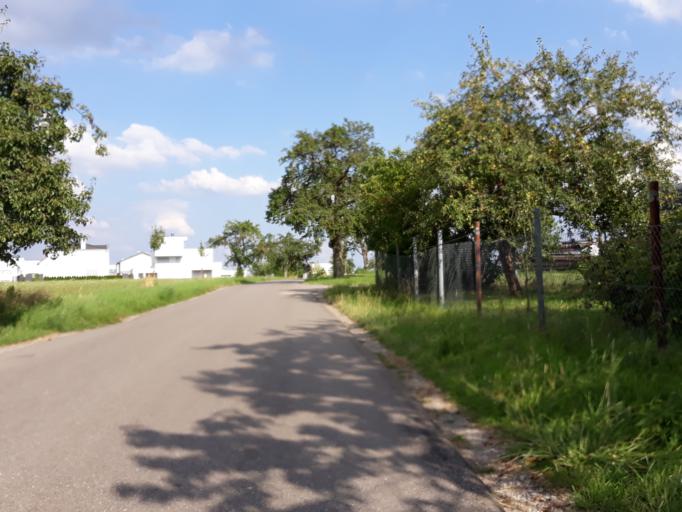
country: DE
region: Baden-Wuerttemberg
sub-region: Regierungsbezirk Stuttgart
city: Schonaich
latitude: 48.6609
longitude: 9.0500
